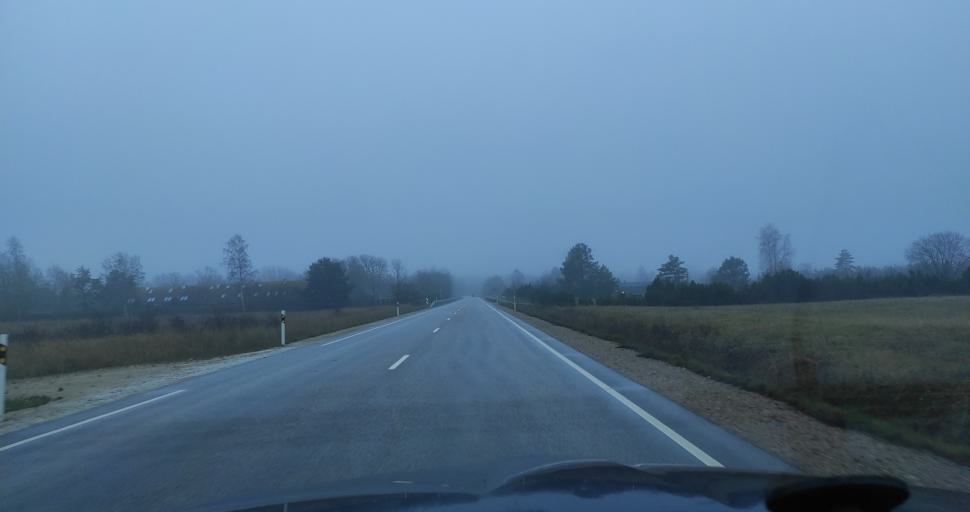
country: LV
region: Pavilostas
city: Pavilosta
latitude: 56.9287
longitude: 21.2693
